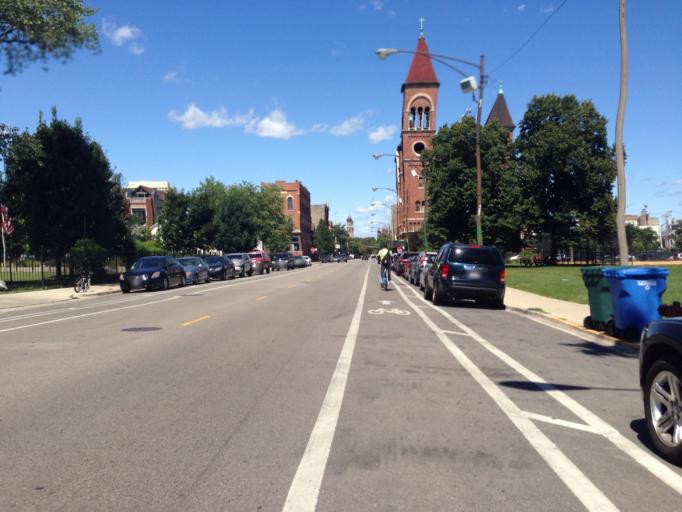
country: US
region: Illinois
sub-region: Cook County
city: Chicago
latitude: 41.8969
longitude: -87.6623
